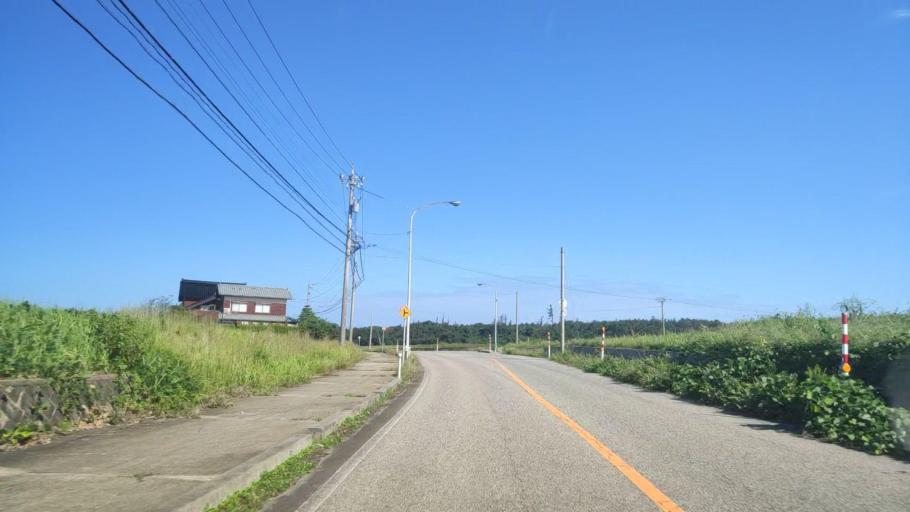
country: JP
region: Ishikawa
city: Hakui
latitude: 37.0338
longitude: 136.7469
